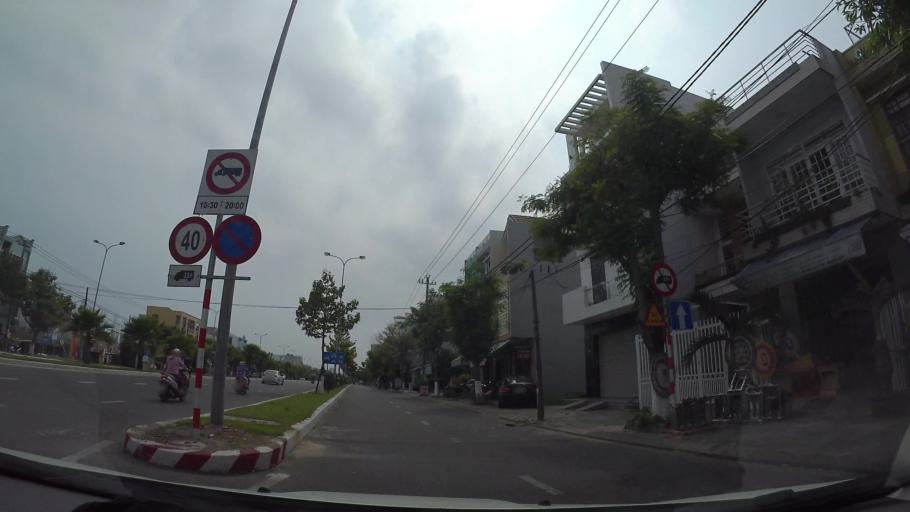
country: VN
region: Da Nang
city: Da Nang
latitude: 16.0927
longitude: 108.2435
